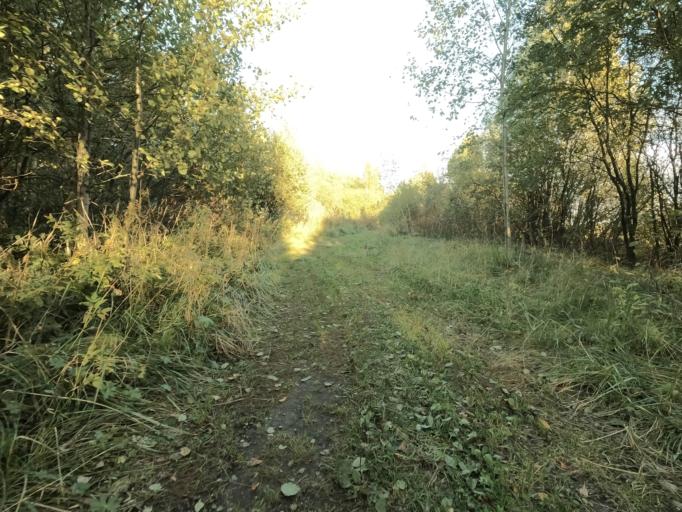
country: RU
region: Leningrad
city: Nikol'skoye
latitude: 59.7010
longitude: 30.7399
